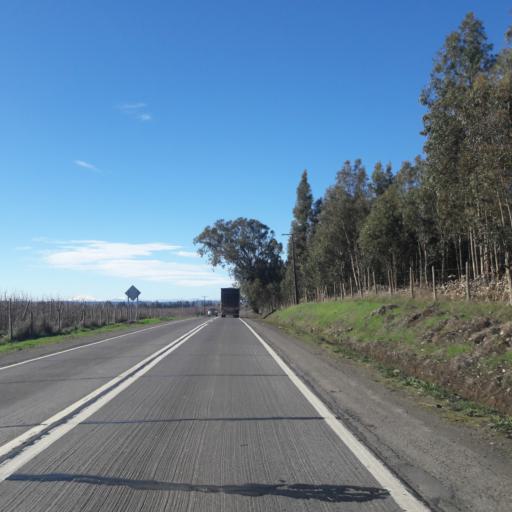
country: CL
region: Araucania
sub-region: Provincia de Malleco
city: Angol
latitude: -37.7442
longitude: -72.6005
